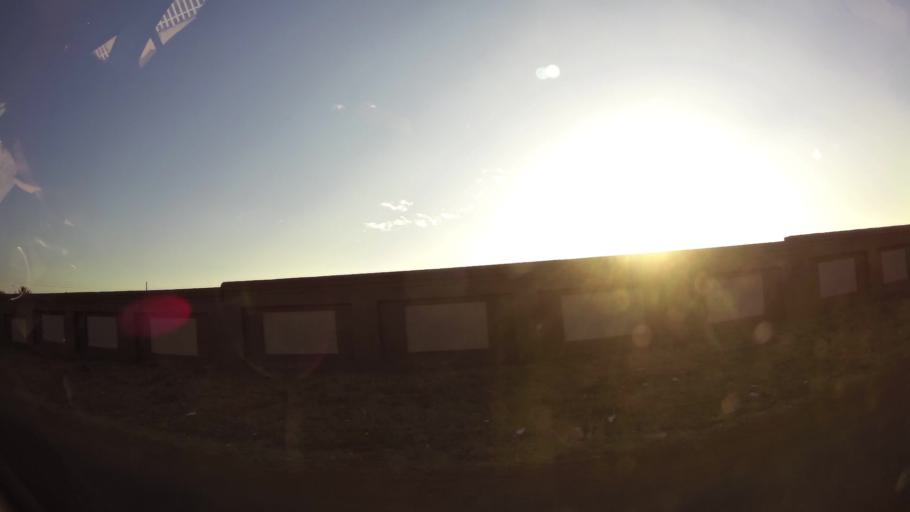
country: ZA
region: Gauteng
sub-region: West Rand District Municipality
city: Randfontein
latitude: -26.2069
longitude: 27.6478
